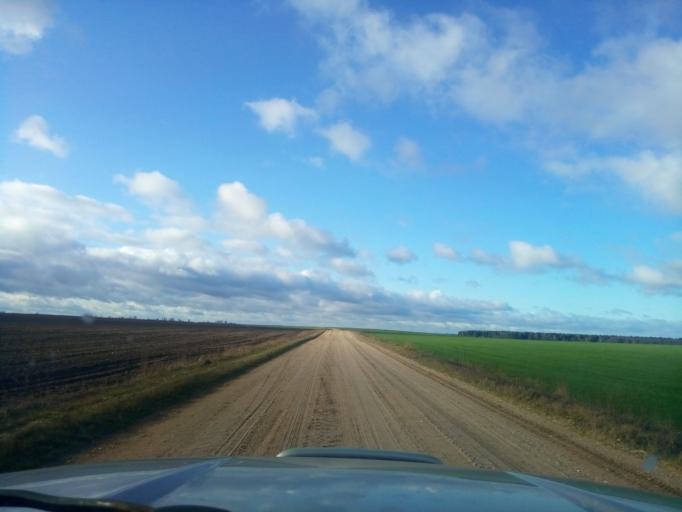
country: BY
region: Minsk
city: Tsimkavichy
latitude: 53.1964
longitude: 26.9168
